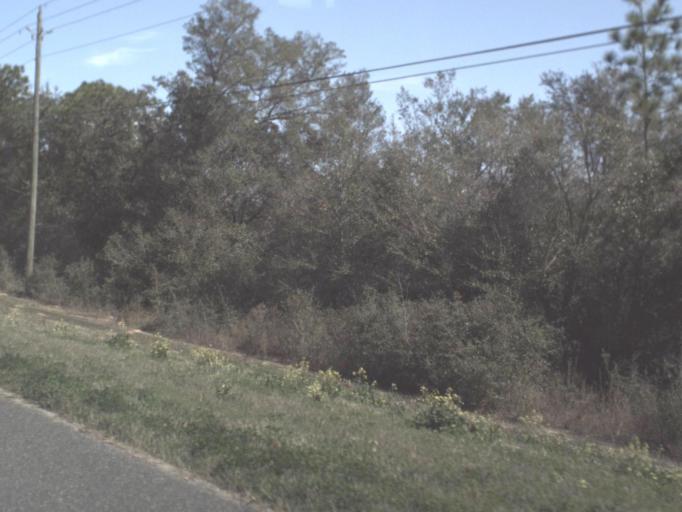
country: US
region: Florida
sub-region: Bay County
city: Lynn Haven
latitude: 30.4225
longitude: -85.6884
